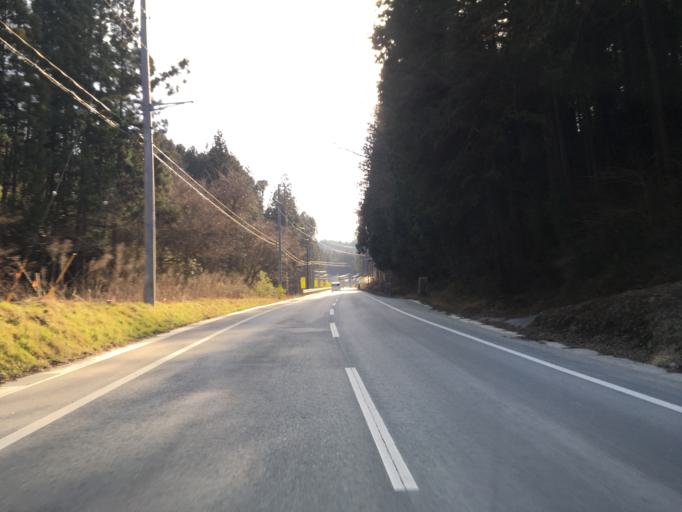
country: JP
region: Ibaraki
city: Daigo
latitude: 36.7135
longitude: 140.4936
